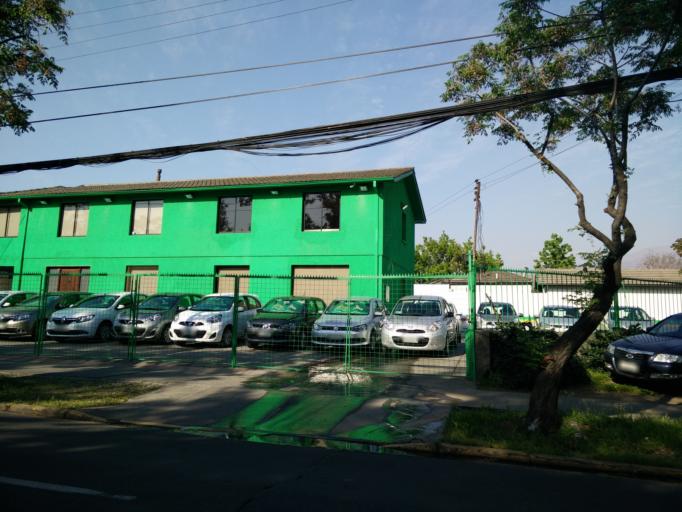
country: CL
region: Santiago Metropolitan
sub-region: Provincia de Santiago
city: Villa Presidente Frei, Nunoa, Santiago, Chile
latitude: -33.4138
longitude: -70.5657
